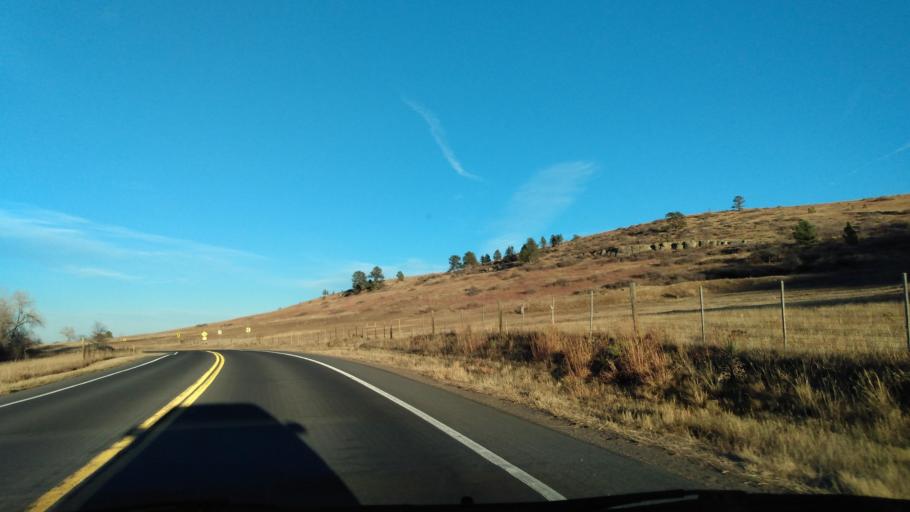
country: US
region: Colorado
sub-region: Boulder County
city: Superior
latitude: 39.9621
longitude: -105.2159
